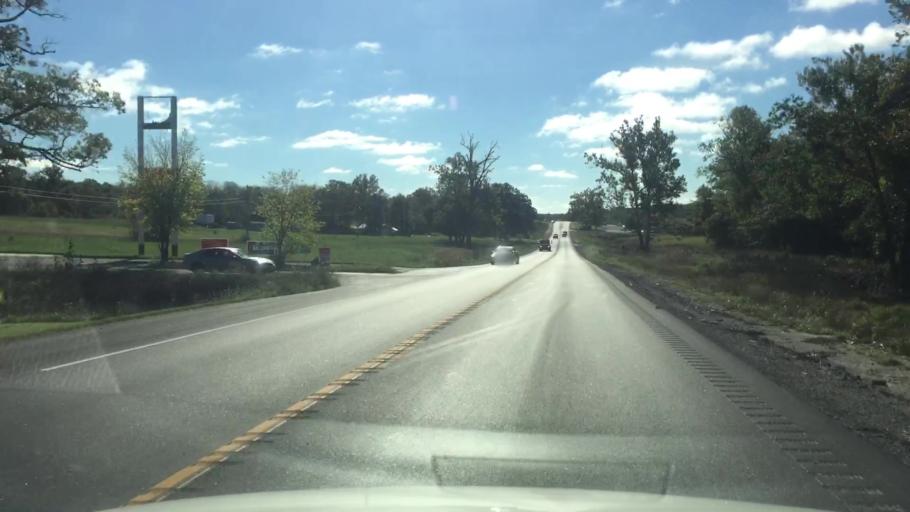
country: US
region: Missouri
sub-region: Boone County
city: Columbia
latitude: 38.9787
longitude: -92.4388
